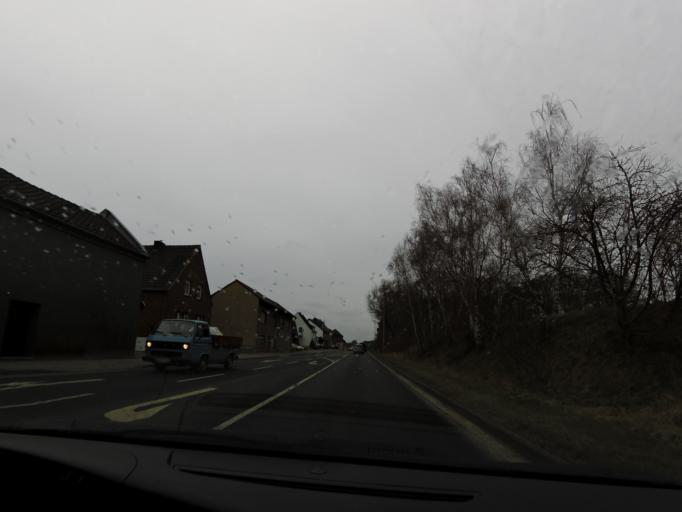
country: DE
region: North Rhine-Westphalia
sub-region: Regierungsbezirk Koln
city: Gangelt
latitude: 50.9836
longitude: 6.0541
